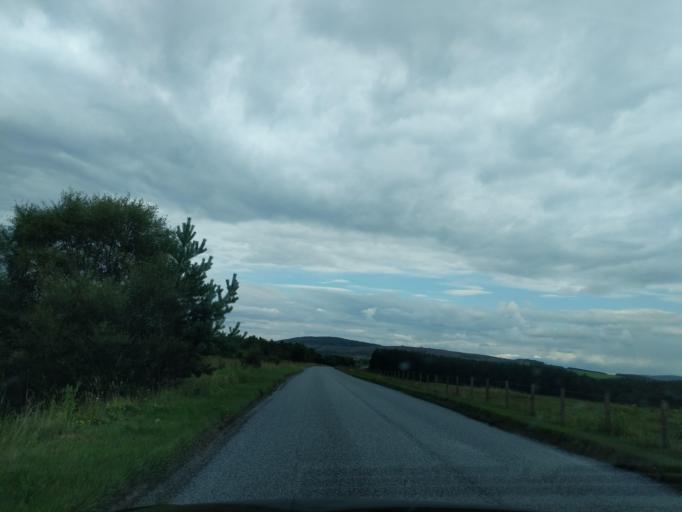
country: GB
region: Scotland
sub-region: Highland
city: Grantown on Spey
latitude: 57.3043
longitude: -3.7456
